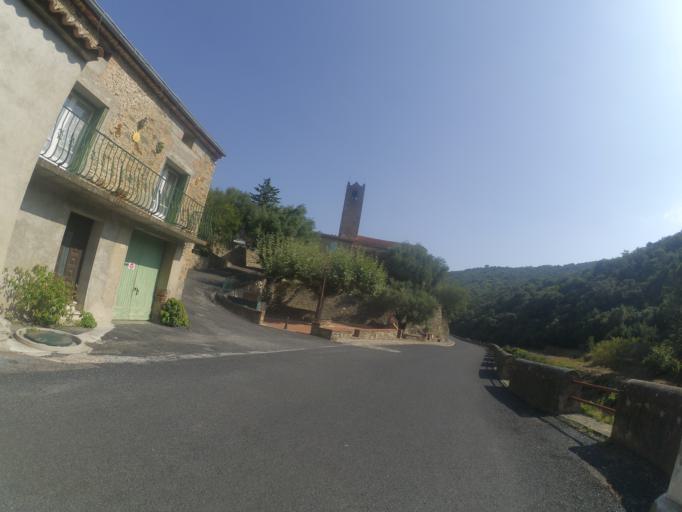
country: FR
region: Languedoc-Roussillon
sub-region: Departement des Pyrenees-Orientales
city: Ille-sur-Tet
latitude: 42.6456
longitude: 2.6242
